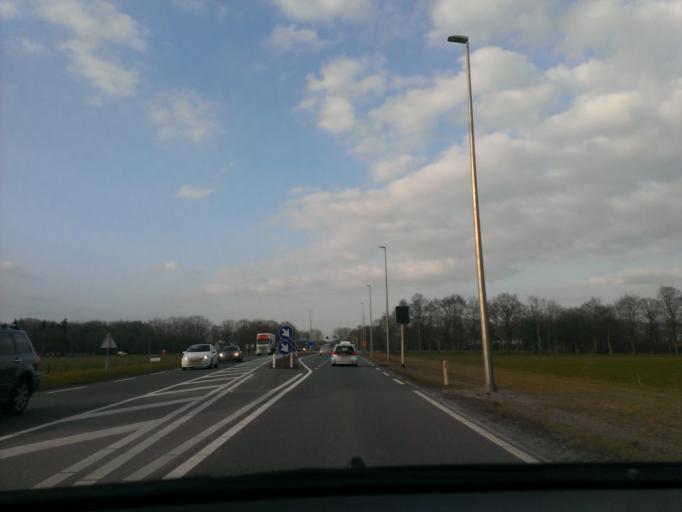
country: NL
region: Overijssel
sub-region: Gemeente Raalte
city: Heino
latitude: 52.4267
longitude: 6.2451
